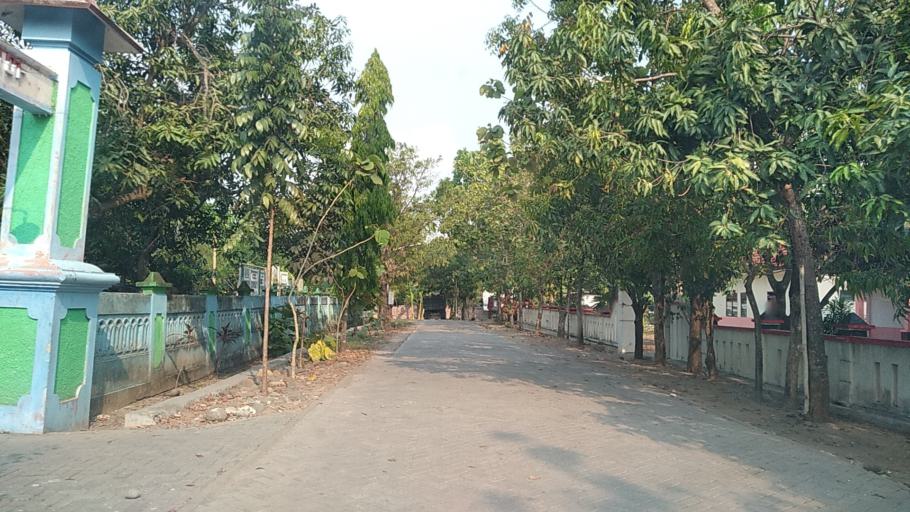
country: ID
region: Central Java
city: Mranggen
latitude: -7.0709
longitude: 110.4737
